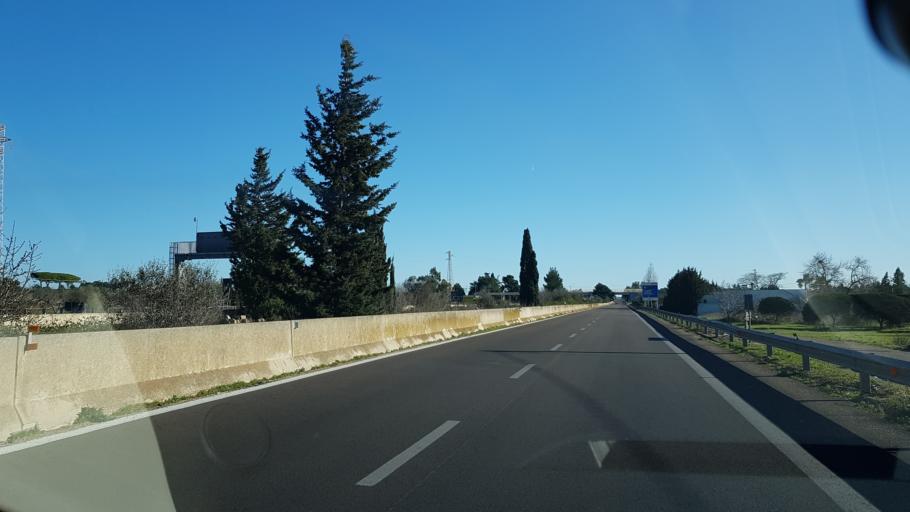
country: IT
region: Apulia
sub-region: Provincia di Lecce
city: Gallipoli
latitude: 40.0361
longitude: 18.0249
